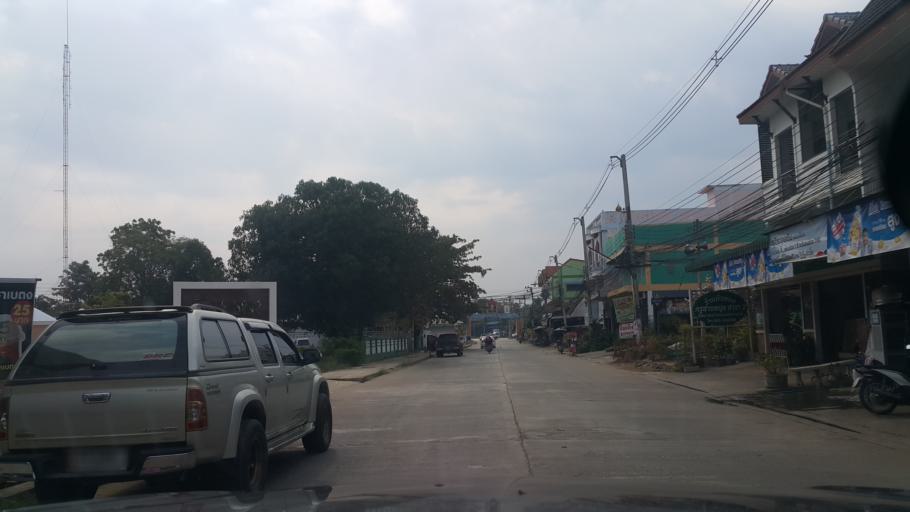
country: TH
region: Sukhothai
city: Si Samrong
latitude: 17.1648
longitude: 99.8609
